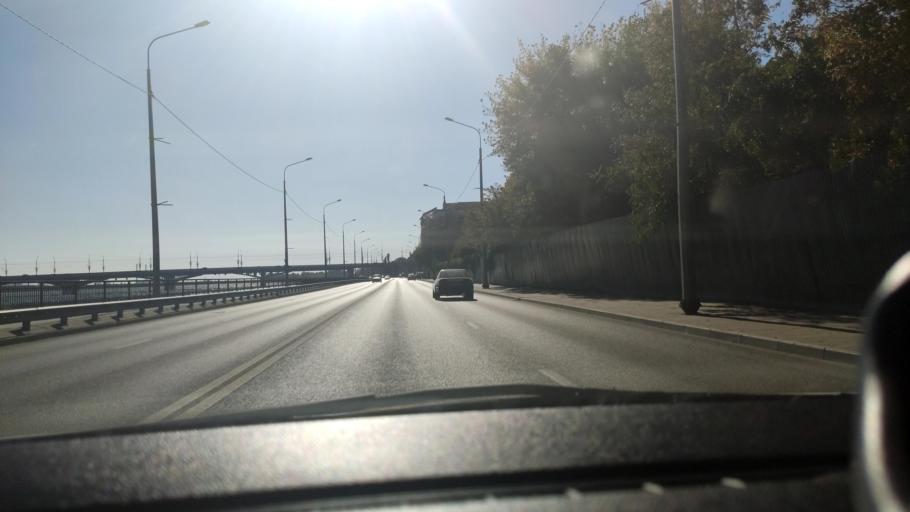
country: RU
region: Voronezj
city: Voronezh
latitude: 51.6720
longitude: 39.2240
